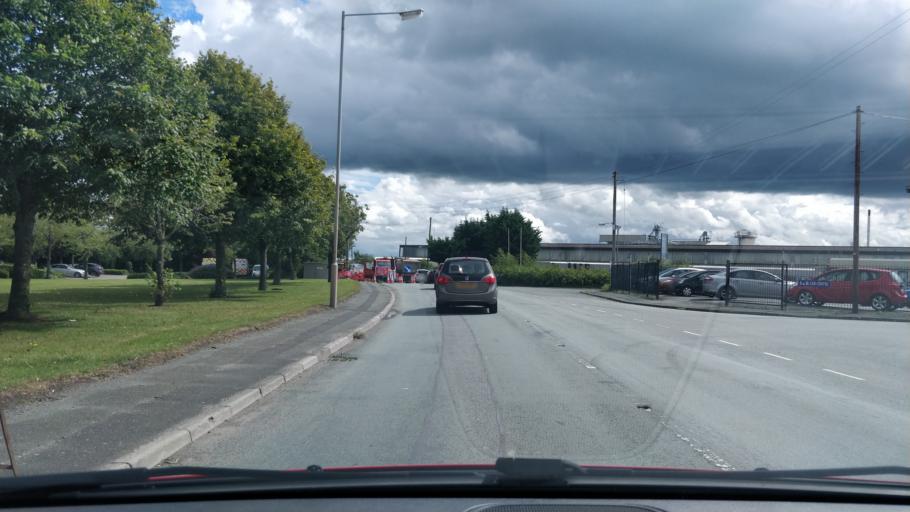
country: GB
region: Wales
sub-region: County of Flintshire
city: Hope
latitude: 53.1031
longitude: -3.0050
